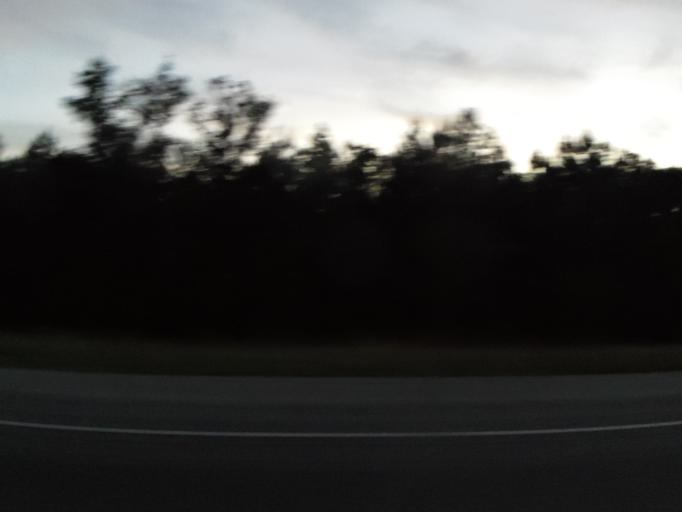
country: US
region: Georgia
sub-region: Liberty County
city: Midway
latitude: 31.6870
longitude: -81.3920
